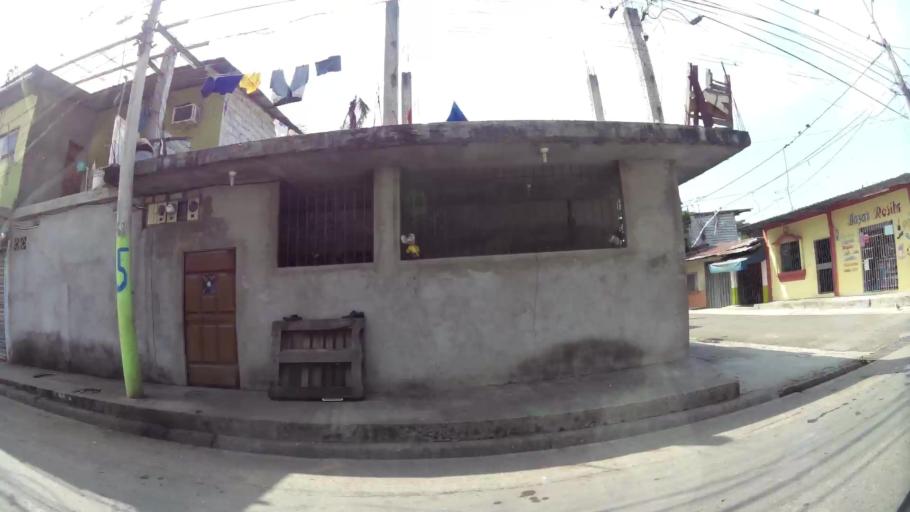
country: EC
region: Guayas
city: Santa Lucia
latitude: -2.1366
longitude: -79.9404
